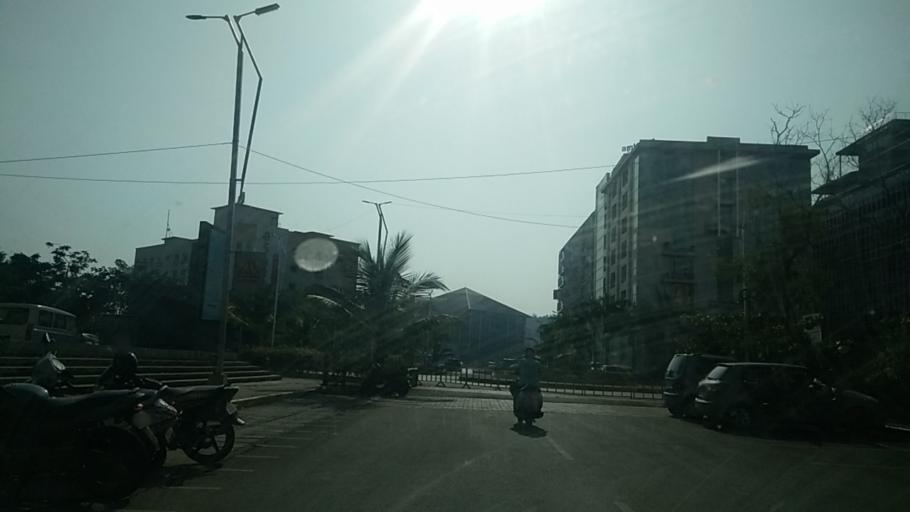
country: IN
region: Goa
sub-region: North Goa
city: Panaji
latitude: 15.4959
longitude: 73.8348
